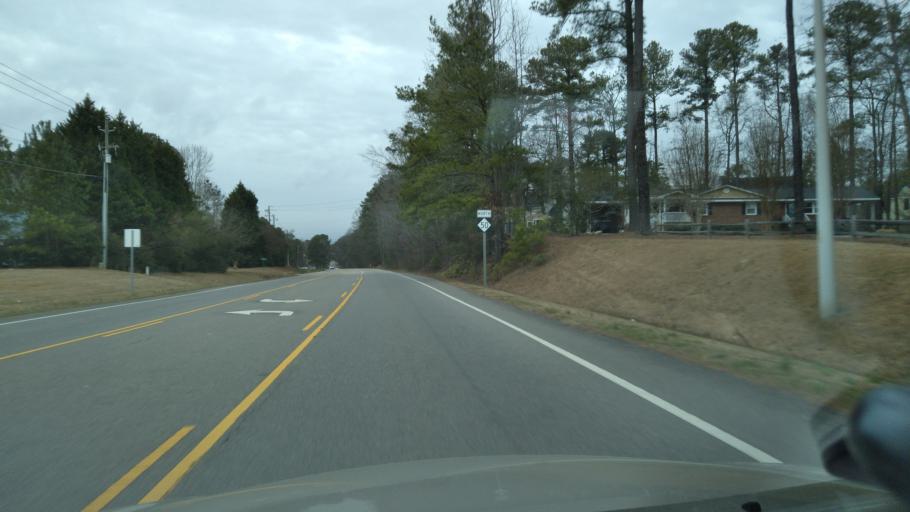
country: US
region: North Carolina
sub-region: Wake County
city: Garner
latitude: 35.6899
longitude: -78.6053
